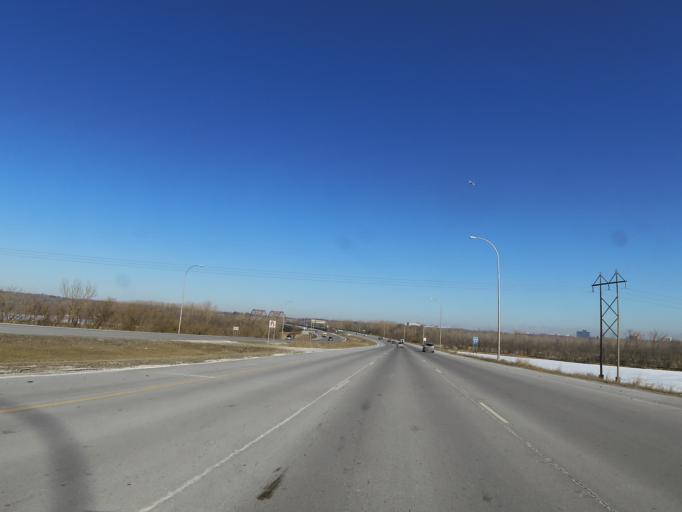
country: US
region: Minnesota
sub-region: Dakota County
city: Eagan
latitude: 44.8207
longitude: -93.2243
